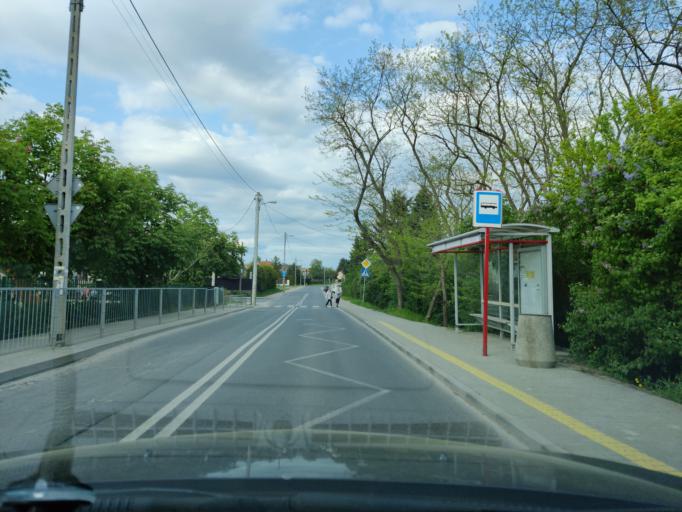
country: PL
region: Masovian Voivodeship
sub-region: Warszawa
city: Kabaty
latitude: 52.1280
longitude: 21.1043
